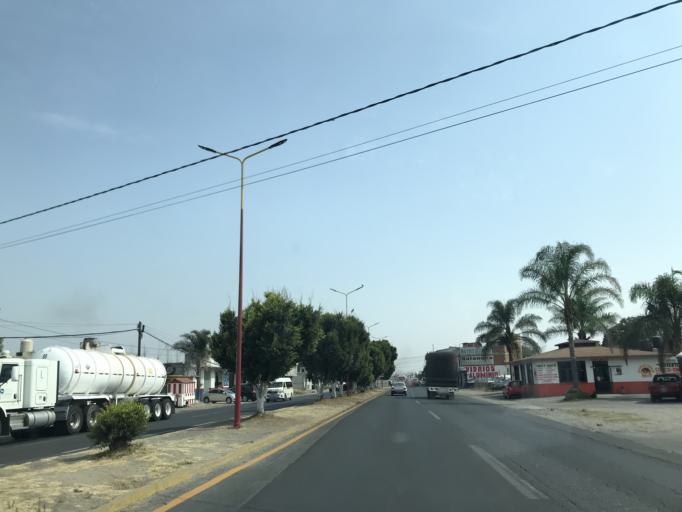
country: MX
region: Tlaxcala
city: La Magdalena Tlaltelulco
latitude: 19.2815
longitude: -98.1964
